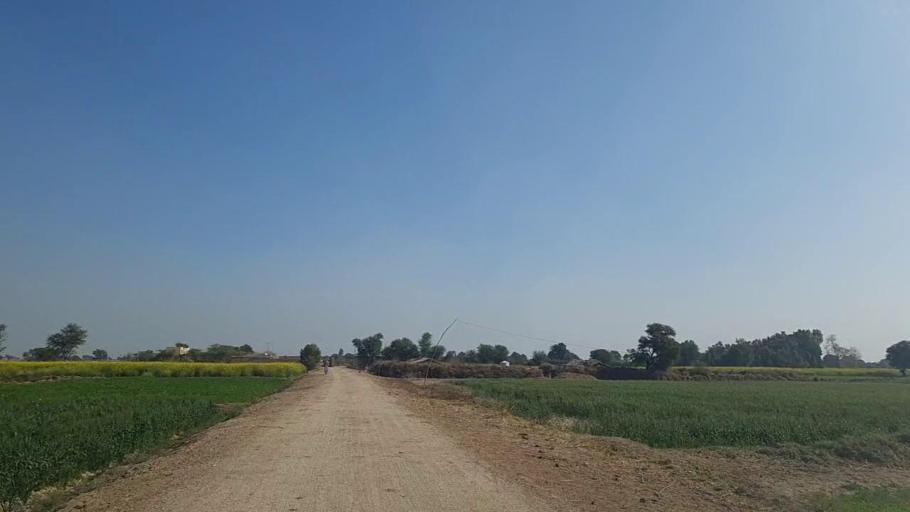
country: PK
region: Sindh
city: Shahpur Chakar
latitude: 26.1916
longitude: 68.6068
